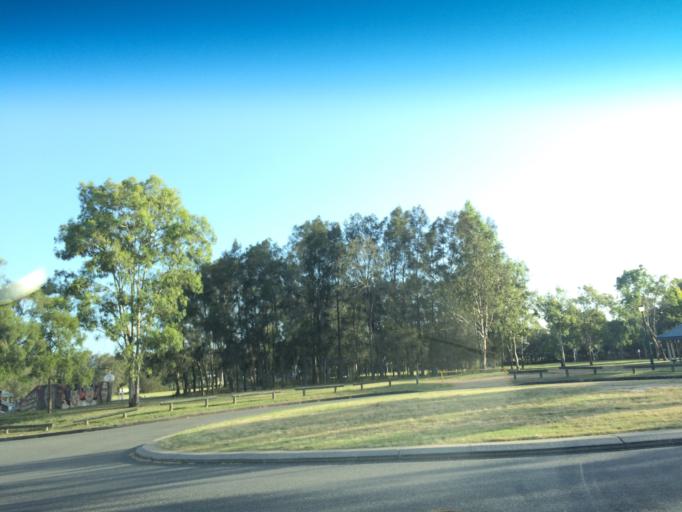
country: AU
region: Queensland
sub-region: Brisbane
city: Woolloongabba
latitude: -27.4890
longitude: 153.0519
